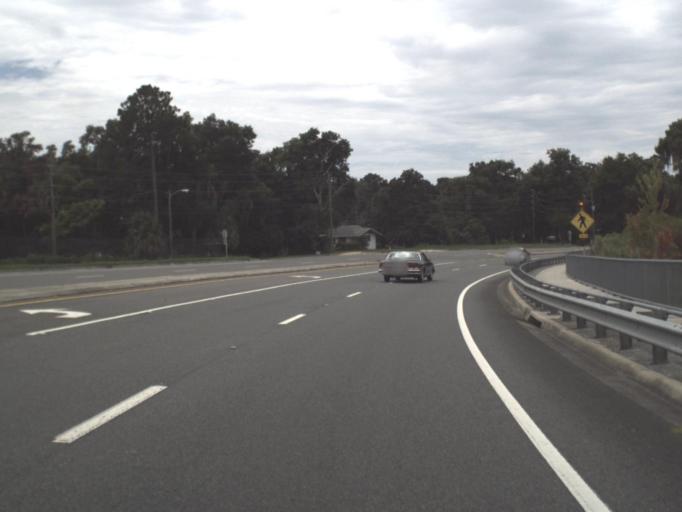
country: US
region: Florida
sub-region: Citrus County
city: Inverness
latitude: 28.8333
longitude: -82.3150
